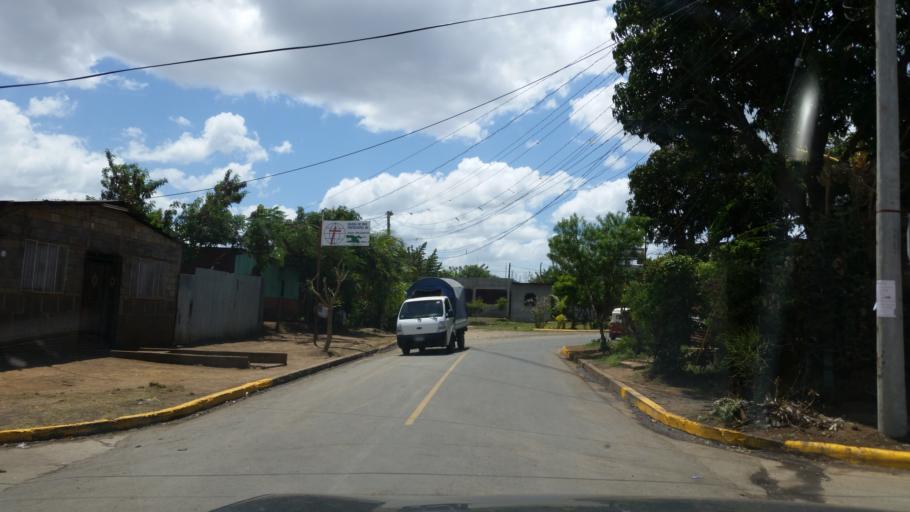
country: NI
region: Managua
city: Managua
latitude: 12.1133
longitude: -86.2079
